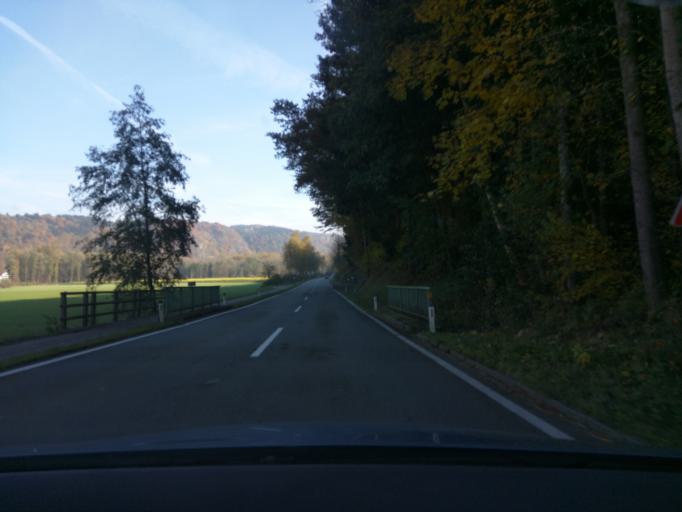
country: DE
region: Bavaria
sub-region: Lower Bavaria
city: Thyrnau
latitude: 48.5858
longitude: 13.5156
